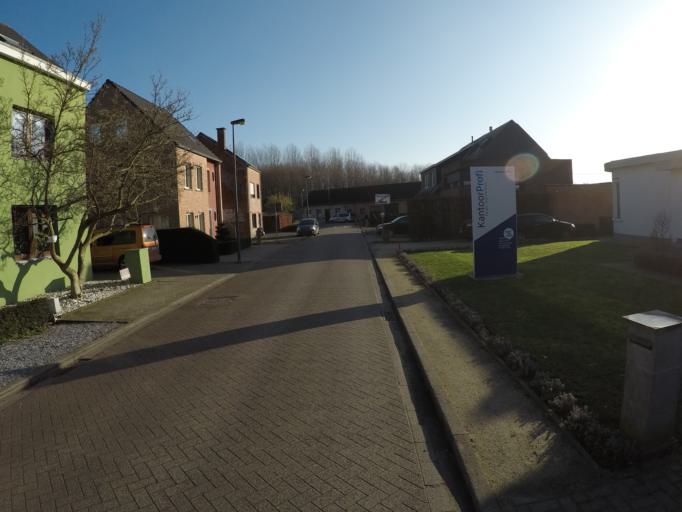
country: BE
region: Flanders
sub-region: Provincie Antwerpen
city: Wommelgem
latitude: 51.2081
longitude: 4.5370
